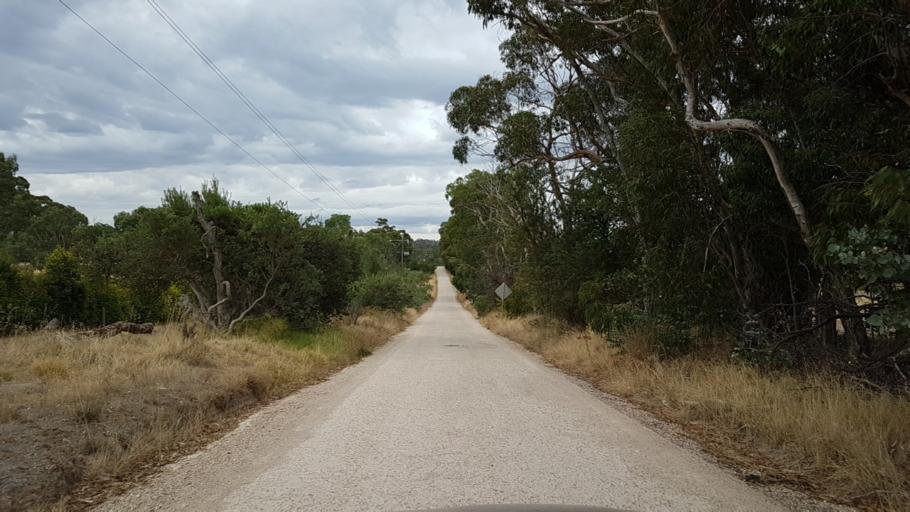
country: AU
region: South Australia
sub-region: Adelaide Hills
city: Gumeracha
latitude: -34.7830
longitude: 138.8632
